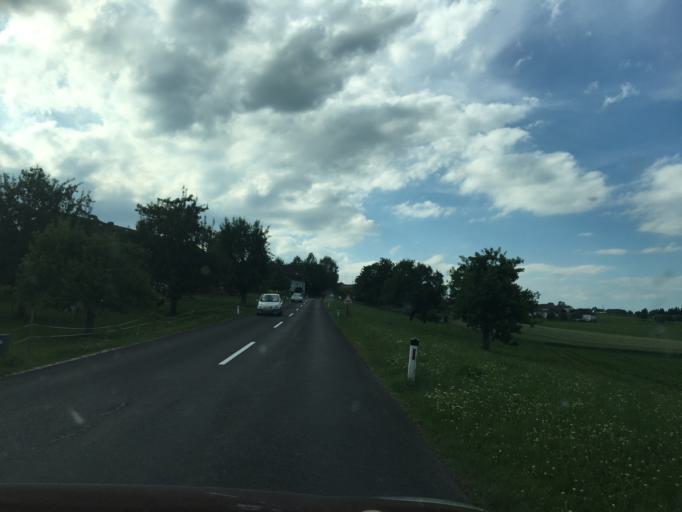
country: AT
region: Upper Austria
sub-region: Politischer Bezirk Urfahr-Umgebung
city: Reichenau im Muhlkreis
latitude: 48.4649
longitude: 14.3435
